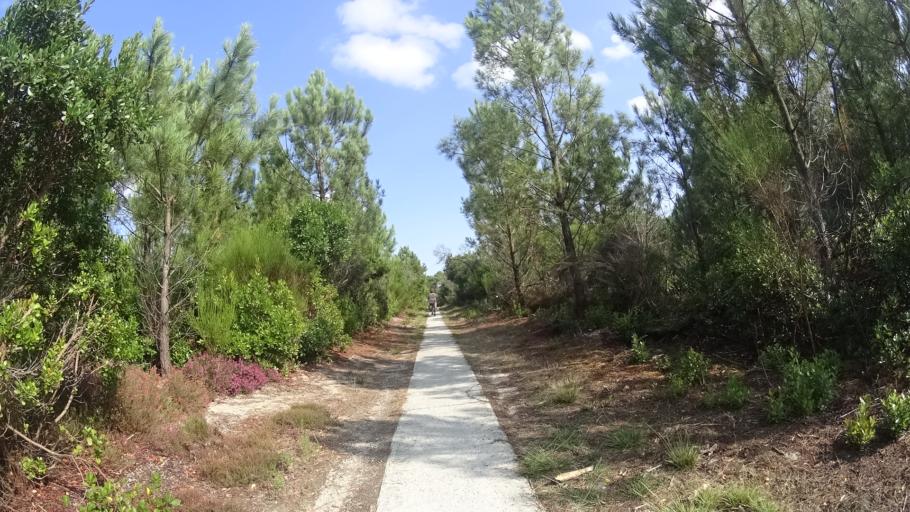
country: FR
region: Aquitaine
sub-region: Departement de la Gironde
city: Lacanau
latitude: 44.9658
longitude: -1.1771
